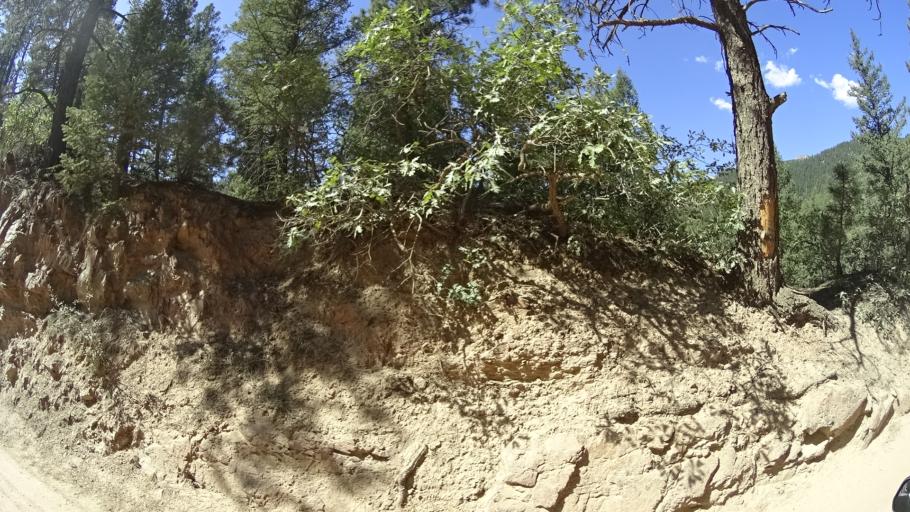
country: US
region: Colorado
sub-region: El Paso County
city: Colorado Springs
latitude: 38.7958
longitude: -104.8817
